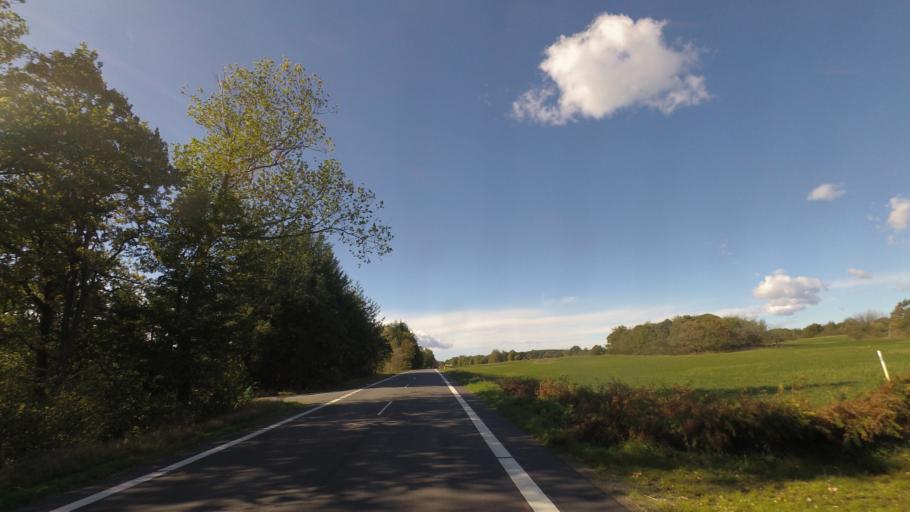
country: DK
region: Capital Region
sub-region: Bornholm Kommune
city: Akirkeby
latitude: 55.0658
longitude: 15.0085
